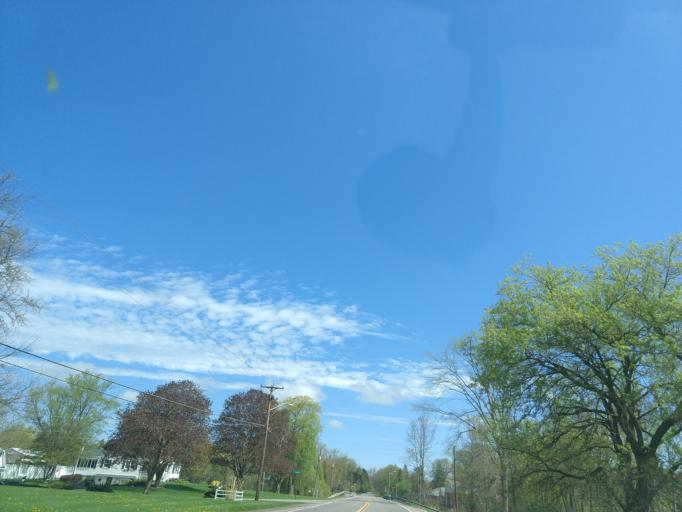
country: US
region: New York
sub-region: Tompkins County
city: Dryden
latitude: 42.5039
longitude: -76.3604
